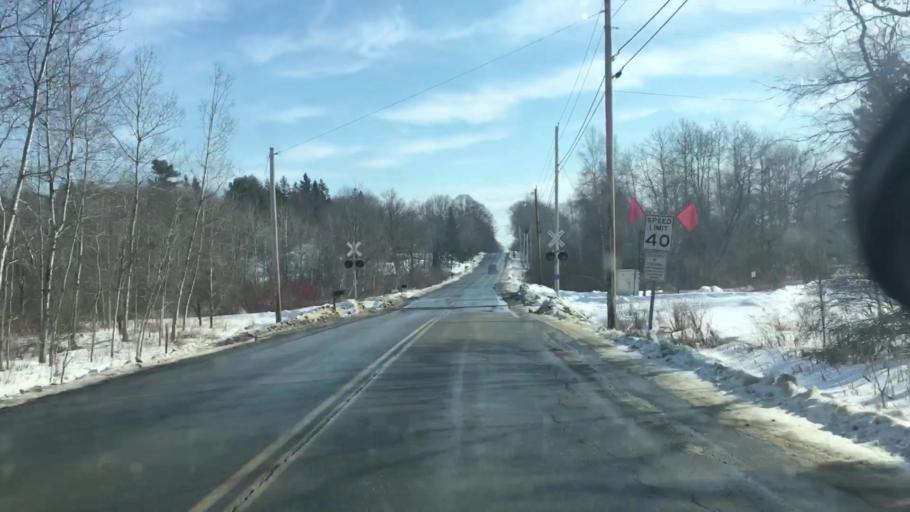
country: US
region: Maine
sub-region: Penobscot County
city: Hermon
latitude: 44.8509
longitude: -68.8427
